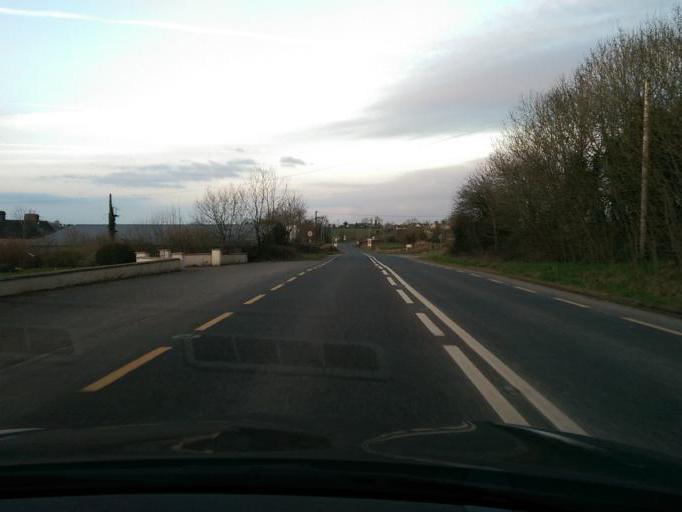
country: IE
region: Munster
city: Nenagh Bridge
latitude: 52.9278
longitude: -8.1668
